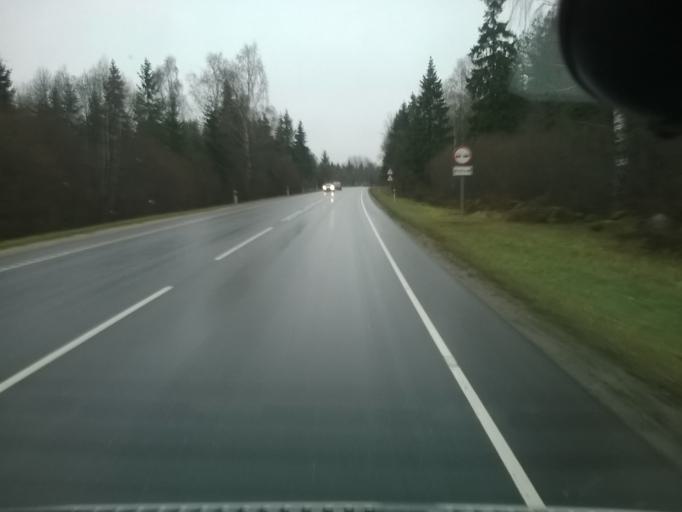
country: EE
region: Harju
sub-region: Nissi vald
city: Turba
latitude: 59.1111
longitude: 24.2583
